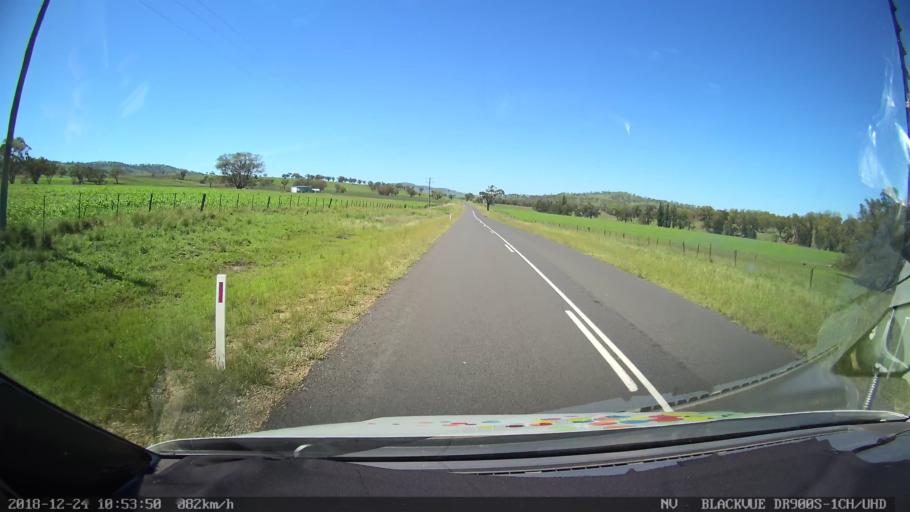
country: AU
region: New South Wales
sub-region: Upper Hunter Shire
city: Merriwa
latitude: -31.9962
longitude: 150.4191
